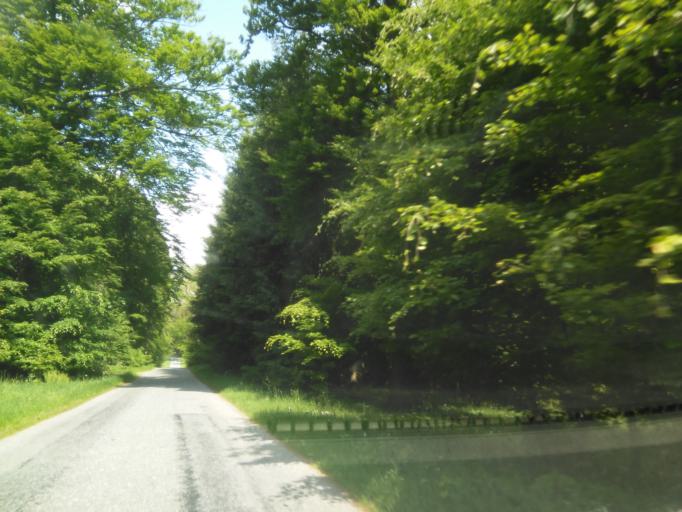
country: DK
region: Central Jutland
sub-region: Skanderborg Kommune
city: Galten
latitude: 56.2199
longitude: 9.9306
